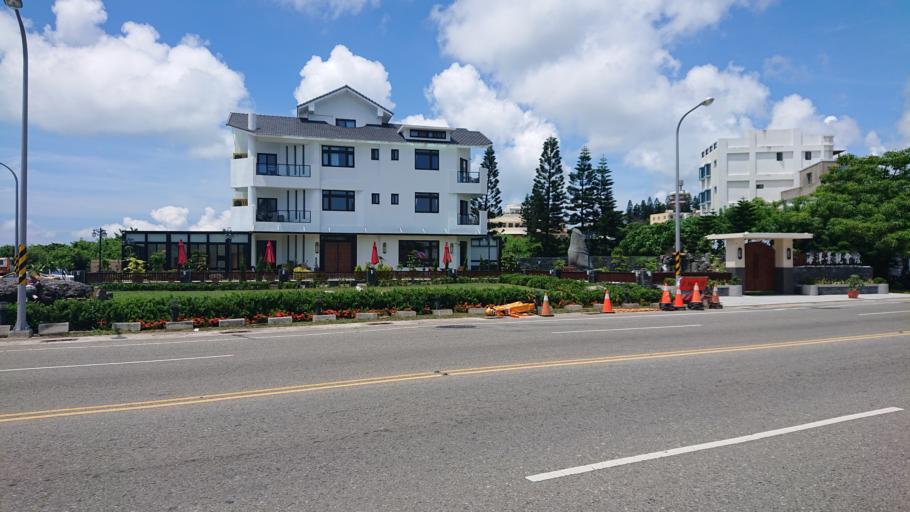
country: TW
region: Taiwan
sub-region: Penghu
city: Ma-kung
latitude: 23.5688
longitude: 119.5978
